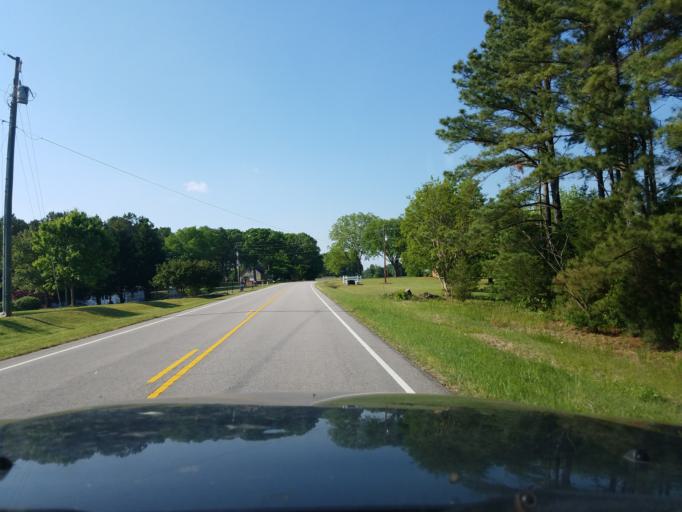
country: US
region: North Carolina
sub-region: Vance County
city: Henderson
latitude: 36.3933
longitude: -78.3683
